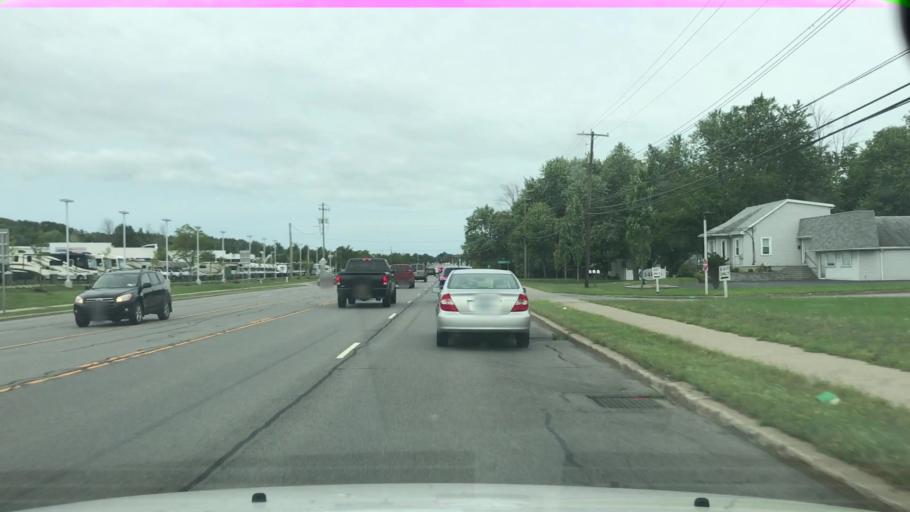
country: US
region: New York
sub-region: Erie County
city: Orchard Park
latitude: 42.7927
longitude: -78.7566
